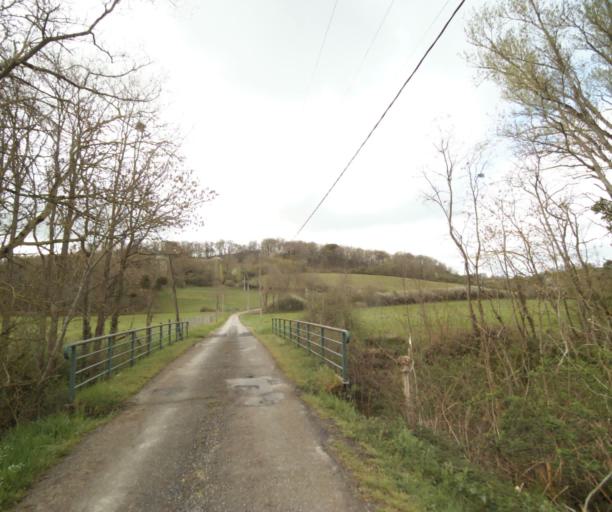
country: FR
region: Midi-Pyrenees
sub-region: Departement de l'Ariege
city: Saverdun
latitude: 43.2259
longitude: 1.5458
